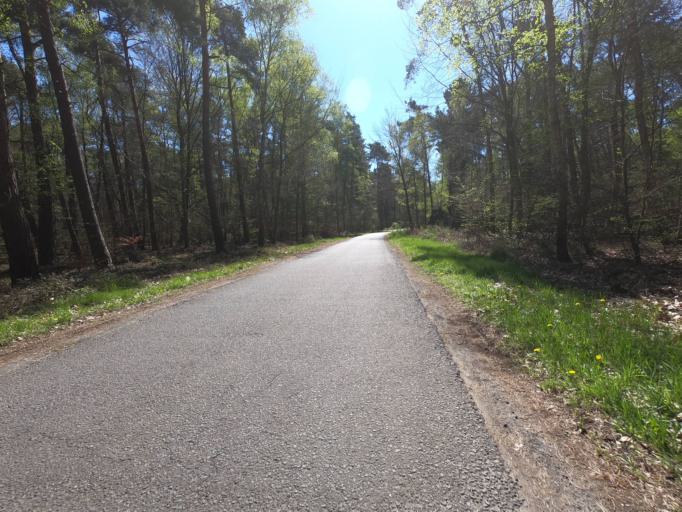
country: DE
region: Hesse
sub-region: Regierungsbezirk Darmstadt
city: Erzhausen
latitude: 49.9428
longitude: 8.6135
